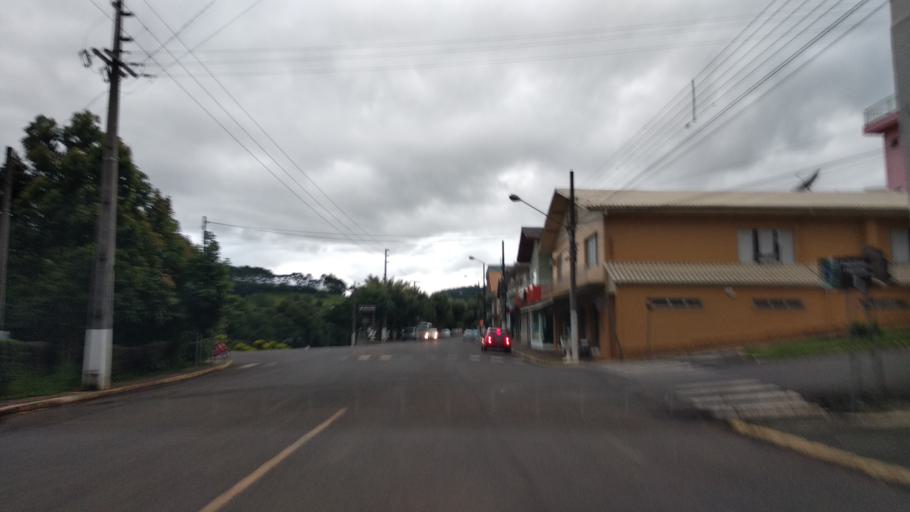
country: BR
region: Santa Catarina
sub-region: Videira
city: Videira
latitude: -27.0469
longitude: -51.2296
